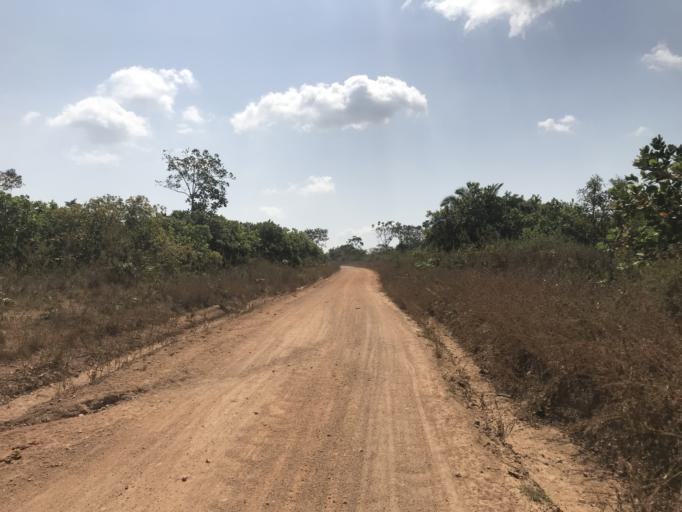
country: NG
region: Osun
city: Ifon
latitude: 7.9282
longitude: 4.4824
